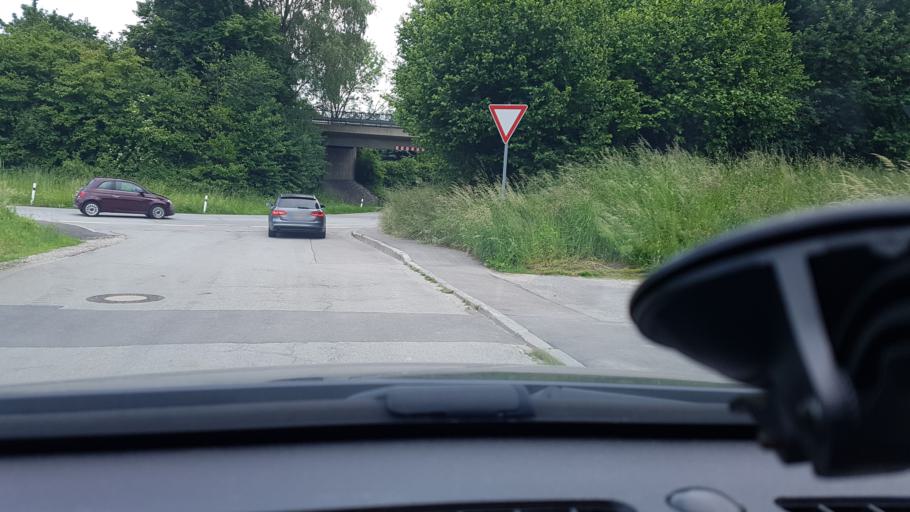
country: AT
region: Upper Austria
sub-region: Politischer Bezirk Braunau am Inn
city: Braunau am Inn
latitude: 48.2745
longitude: 13.0438
